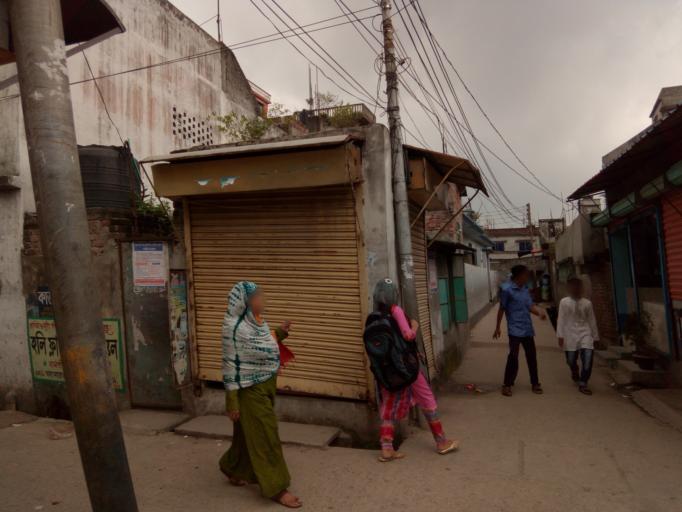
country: BD
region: Dhaka
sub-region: Dhaka
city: Dhaka
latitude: 23.6922
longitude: 90.4452
